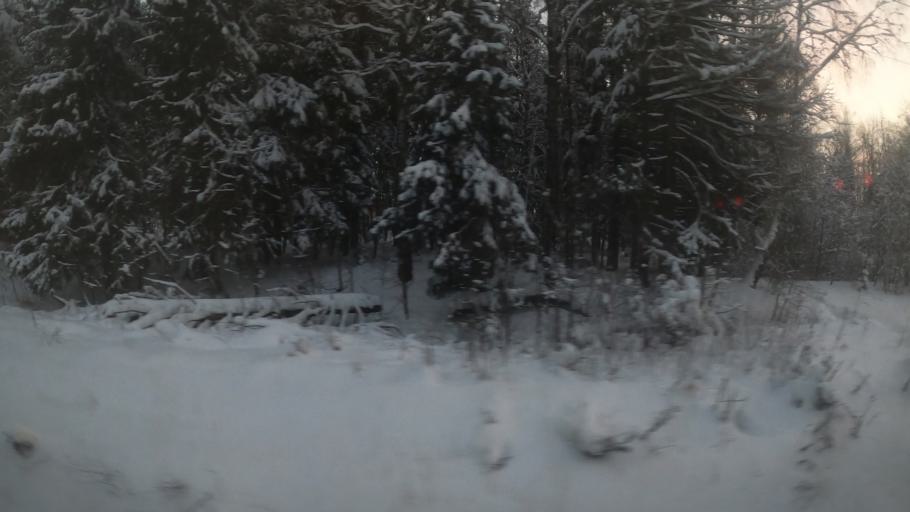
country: RU
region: Moskovskaya
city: Lugovaya
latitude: 56.0568
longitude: 37.4873
